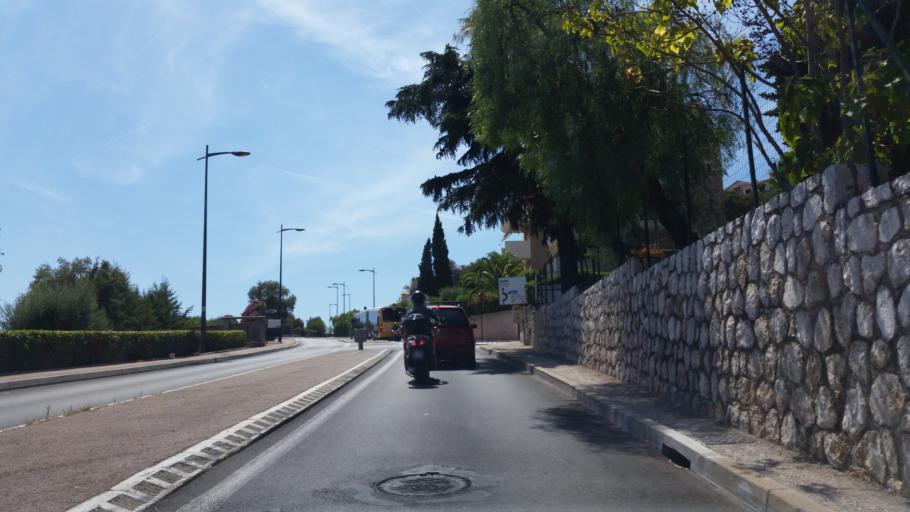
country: FR
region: Provence-Alpes-Cote d'Azur
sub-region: Departement des Alpes-Maritimes
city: Roquebrune-Cap-Martin
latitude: 43.7612
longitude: 7.4709
